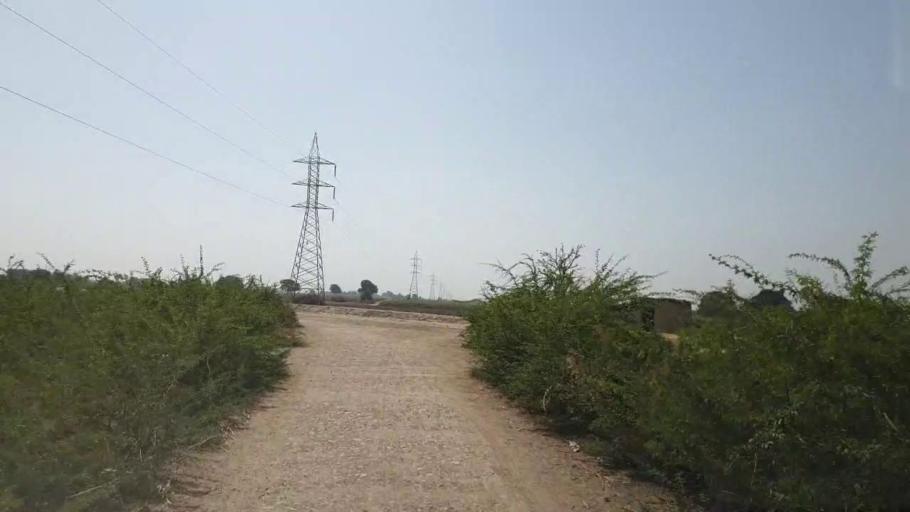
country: PK
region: Sindh
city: Naukot
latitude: 24.9846
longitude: 69.4741
